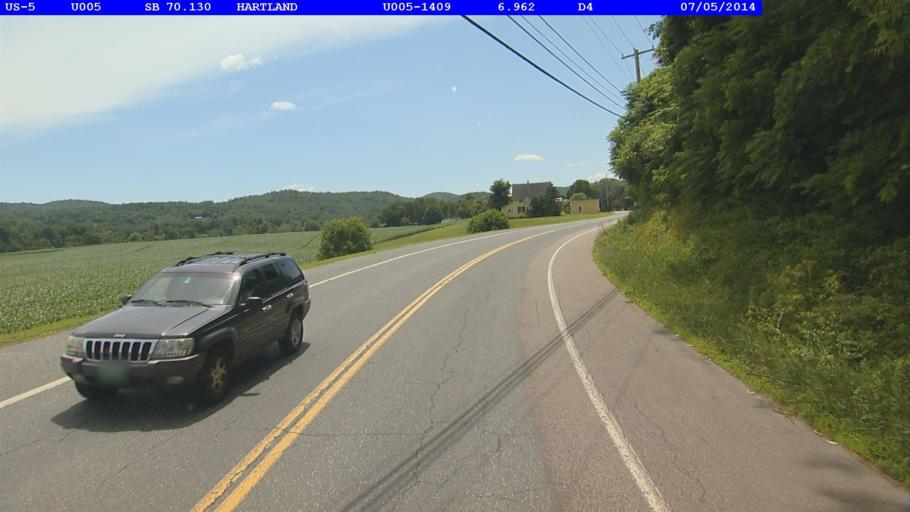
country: US
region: Vermont
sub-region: Windsor County
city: White River Junction
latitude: 43.6008
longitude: -72.3536
